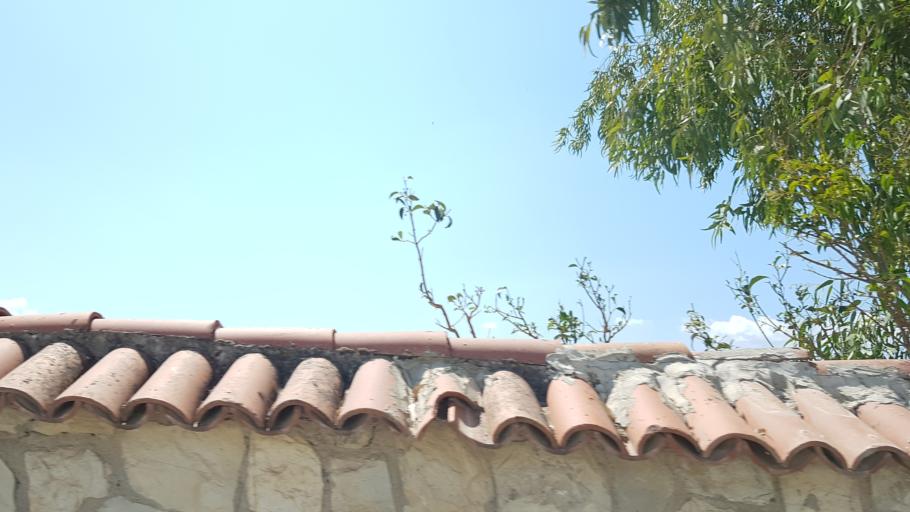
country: TR
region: Izmir
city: Urla
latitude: 38.2828
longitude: 26.7356
